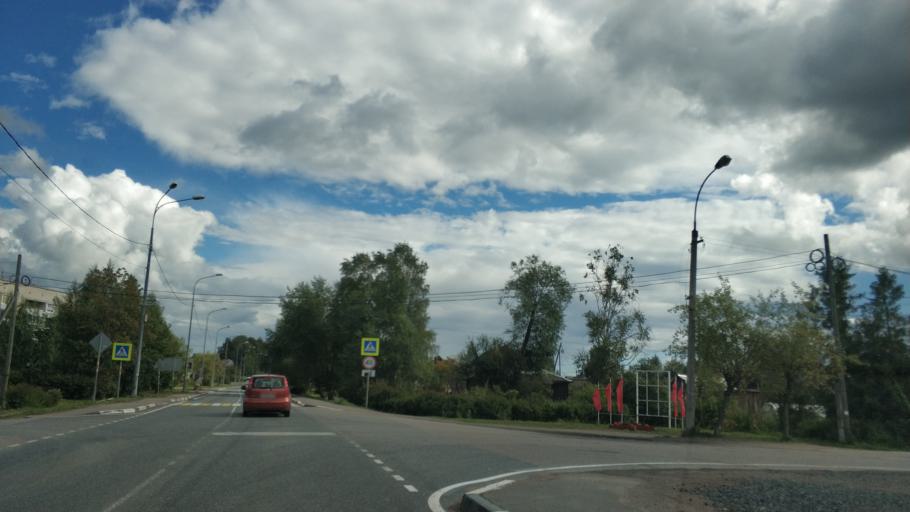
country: RU
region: Republic of Karelia
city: Khelyulya
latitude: 61.7475
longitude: 30.6675
